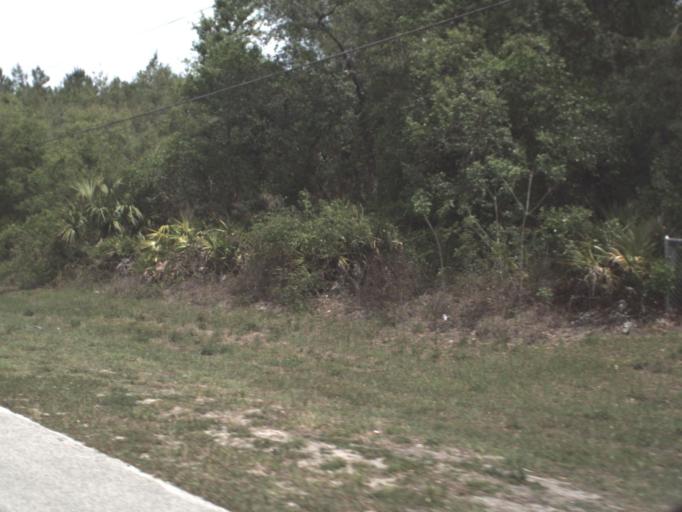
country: US
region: Florida
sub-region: Lake County
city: Lake Mack-Forest Hills
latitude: 28.9501
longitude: -81.4228
